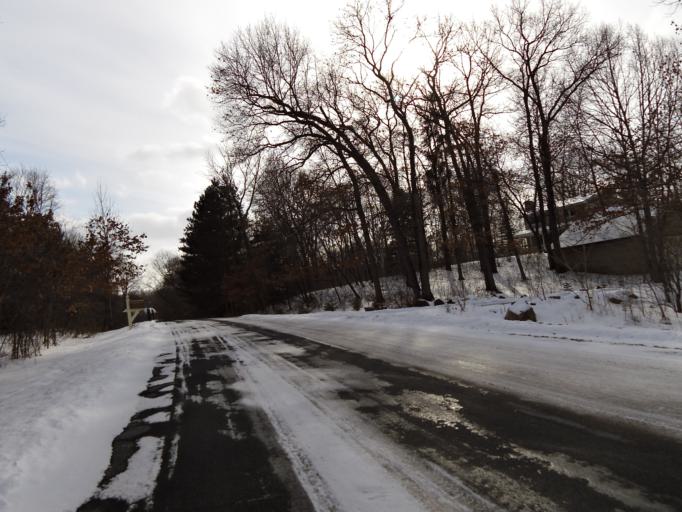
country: US
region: Minnesota
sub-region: Washington County
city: Lake Elmo
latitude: 44.9659
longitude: -92.8338
